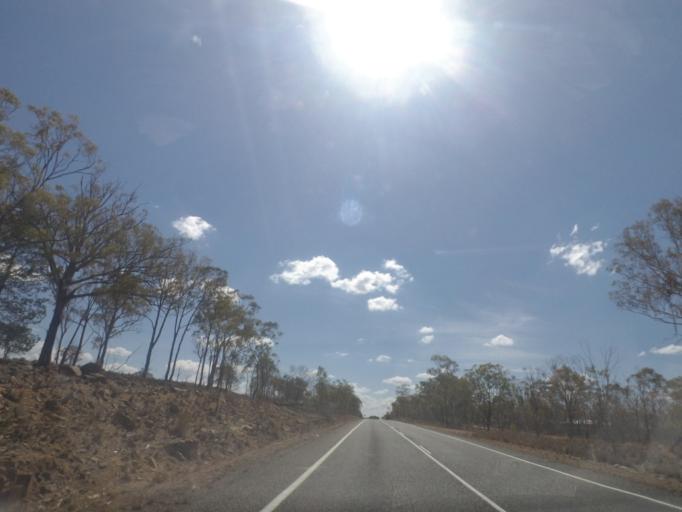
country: AU
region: Queensland
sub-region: Southern Downs
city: Warwick
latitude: -28.2056
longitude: 151.5775
